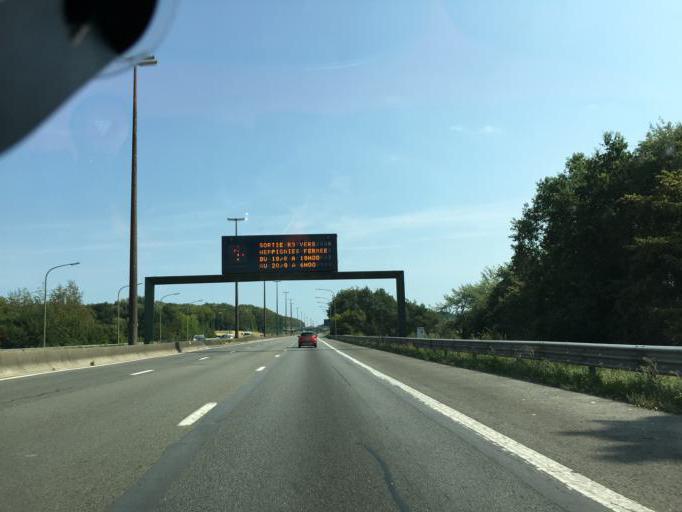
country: BE
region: Wallonia
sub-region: Province du Hainaut
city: Chapelle-lez-Herlaimont
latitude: 50.4908
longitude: 4.2620
